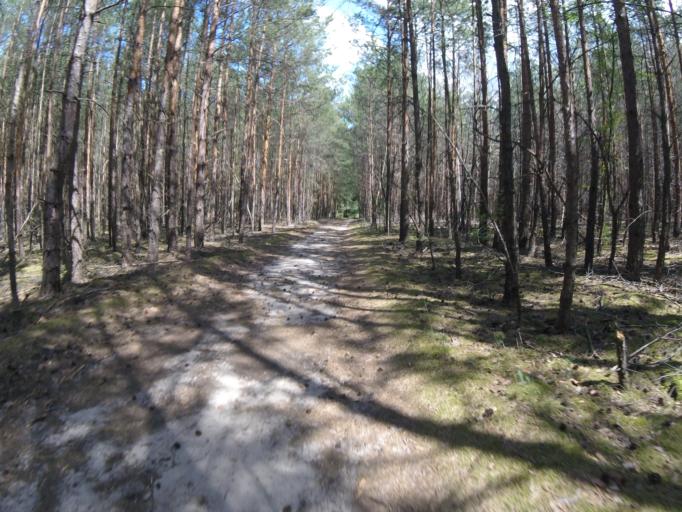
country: DE
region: Brandenburg
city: Bestensee
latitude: 52.2146
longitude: 13.6423
